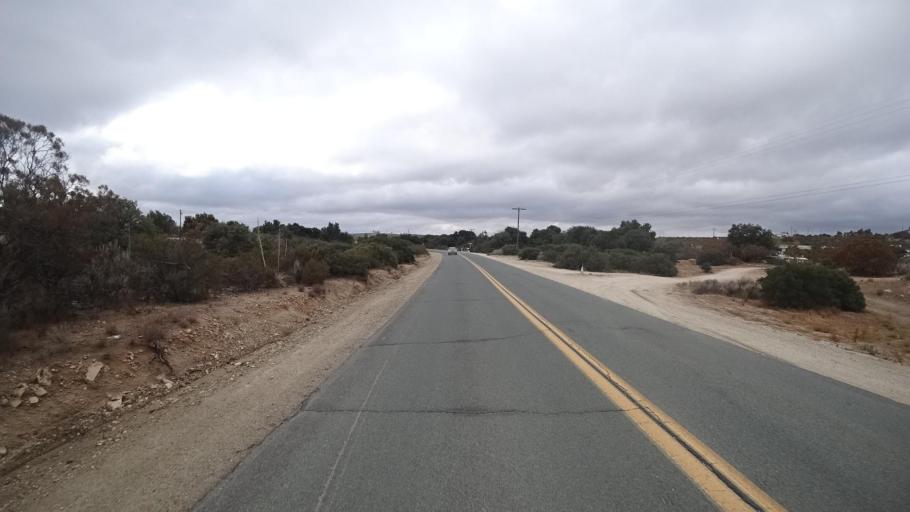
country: US
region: California
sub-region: San Diego County
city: Campo
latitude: 32.6272
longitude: -116.3236
